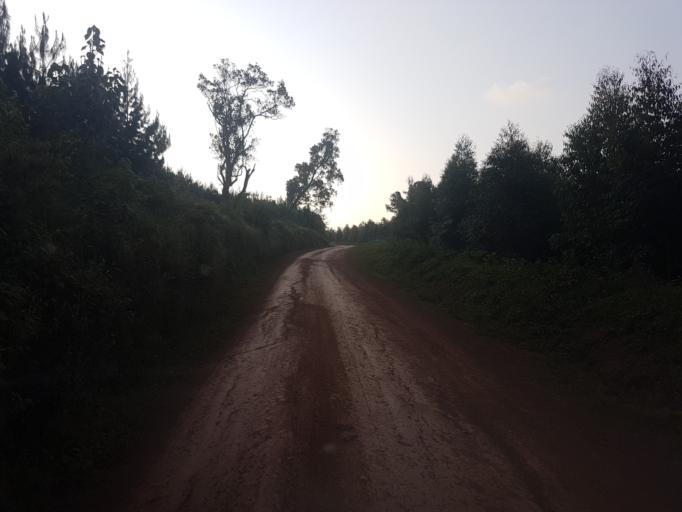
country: UG
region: Western Region
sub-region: Kanungu District
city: Kanungu
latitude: -1.0152
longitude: 29.8630
